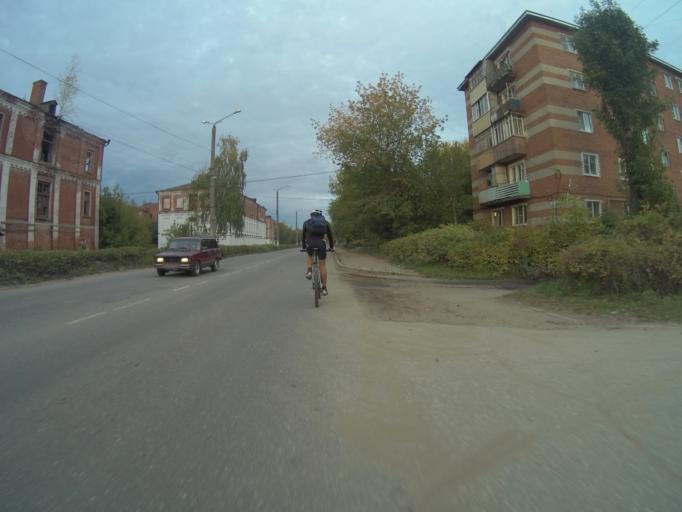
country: RU
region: Vladimir
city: Sobinka
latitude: 55.9911
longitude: 40.0123
